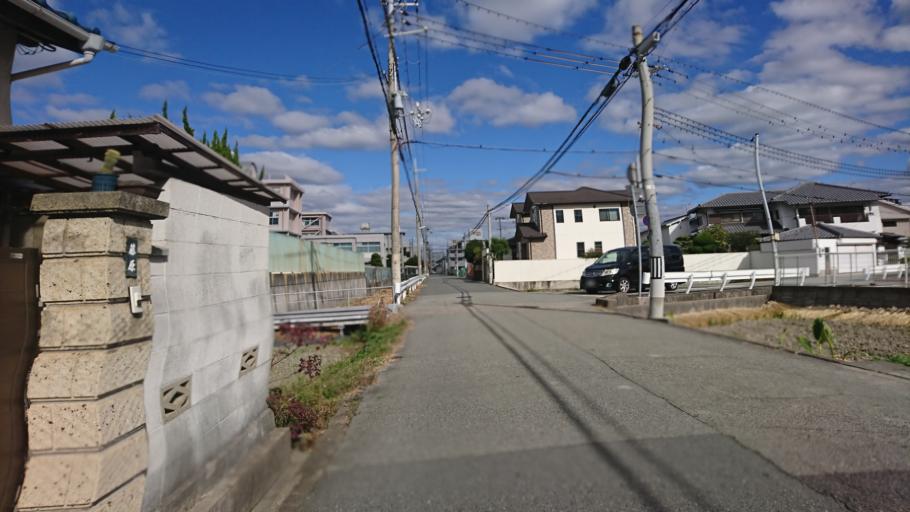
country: JP
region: Hyogo
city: Kakogawacho-honmachi
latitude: 34.7605
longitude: 134.8383
